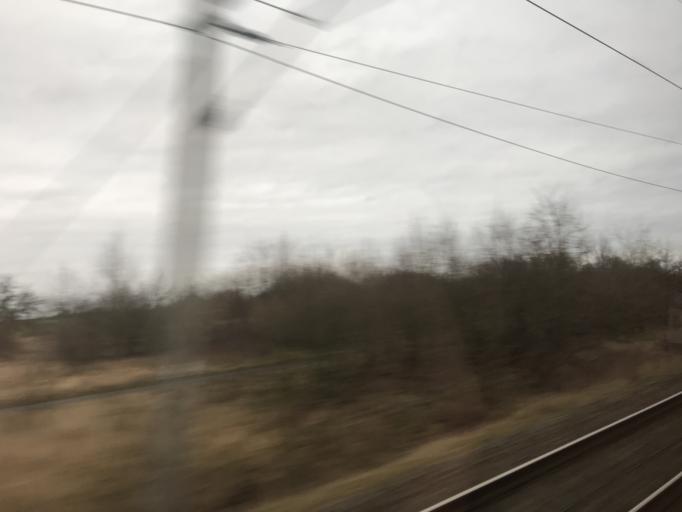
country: DE
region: Saxony-Anhalt
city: Schonhausen
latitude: 52.5998
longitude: 11.9909
